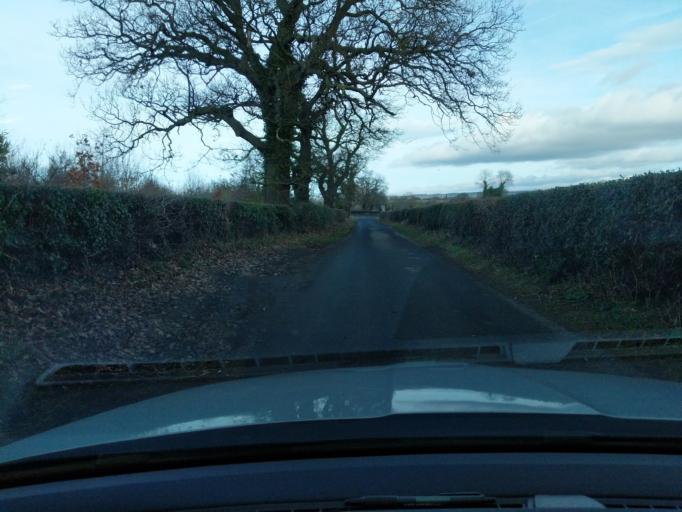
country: GB
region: England
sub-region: North Yorkshire
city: Catterick
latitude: 54.3795
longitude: -1.6719
